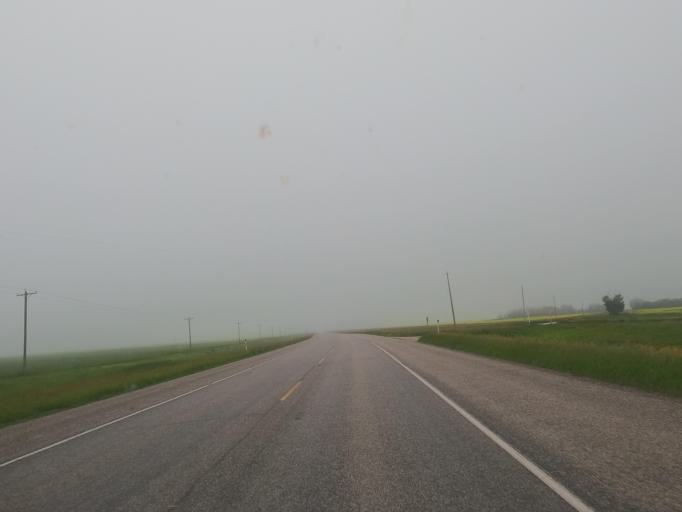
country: CA
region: Manitoba
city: Carman
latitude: 49.7096
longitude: -97.9227
